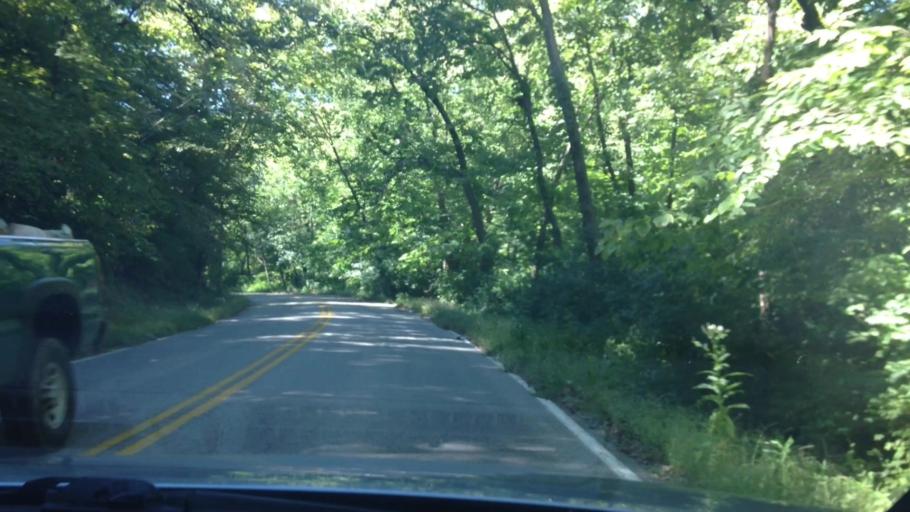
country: US
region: Missouri
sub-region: Jackson County
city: Raytown
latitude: 39.0049
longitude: -94.5161
